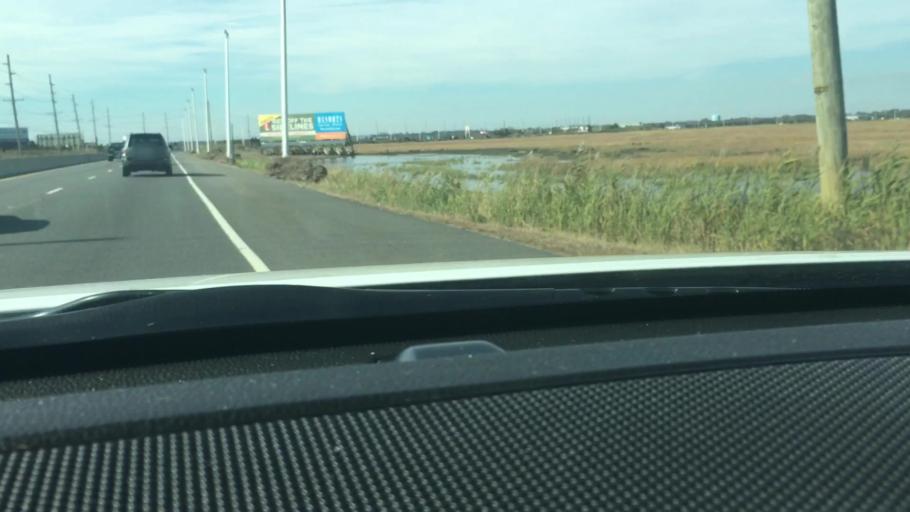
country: US
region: New Jersey
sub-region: Atlantic County
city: Absecon
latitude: 39.3894
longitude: -74.4825
